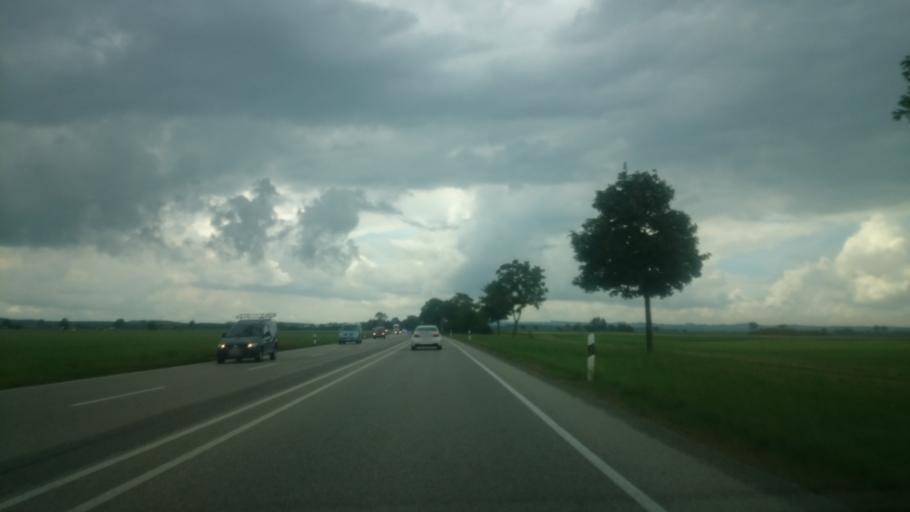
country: DE
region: Bavaria
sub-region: Swabia
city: Rieden
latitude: 47.9447
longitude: 10.6689
